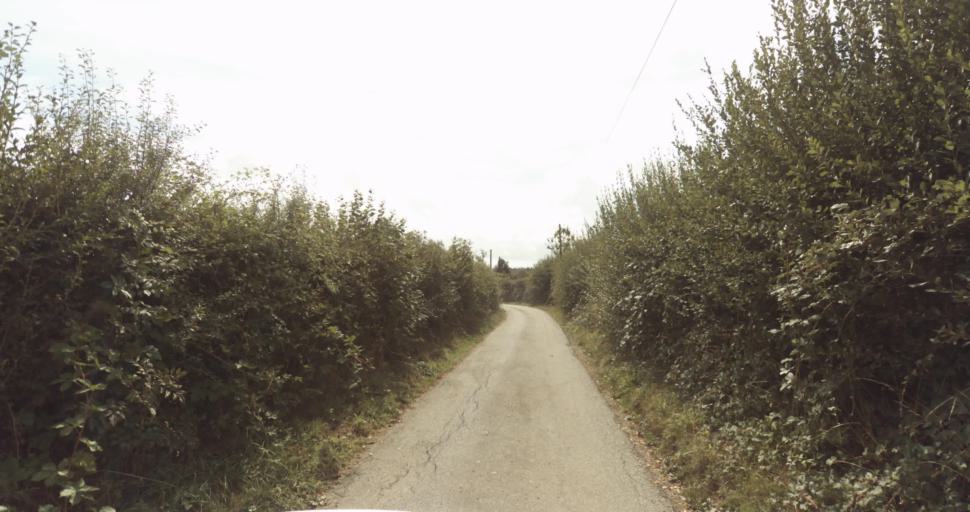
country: FR
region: Lower Normandy
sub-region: Departement de l'Orne
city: Sainte-Gauburge-Sainte-Colombe
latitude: 48.7974
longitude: 0.3985
